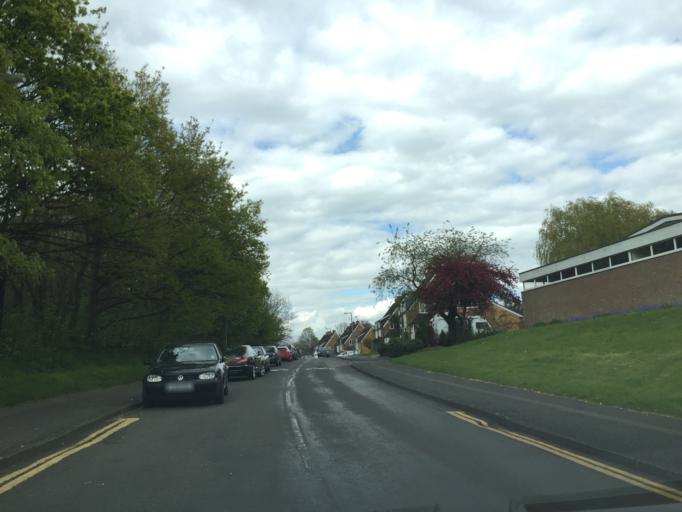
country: GB
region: England
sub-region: Essex
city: Harlow
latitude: 51.7708
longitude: 0.0799
